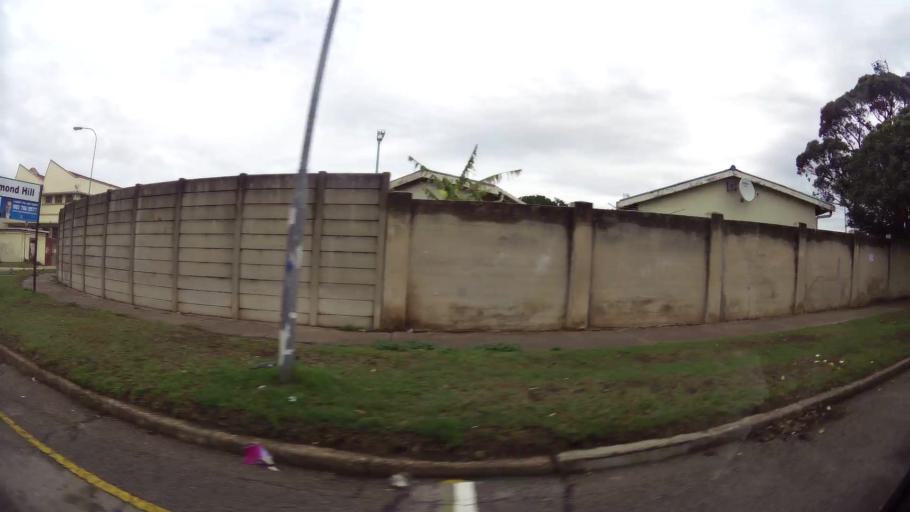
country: ZA
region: Eastern Cape
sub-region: Nelson Mandela Bay Metropolitan Municipality
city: Port Elizabeth
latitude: -33.9606
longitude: 25.6104
